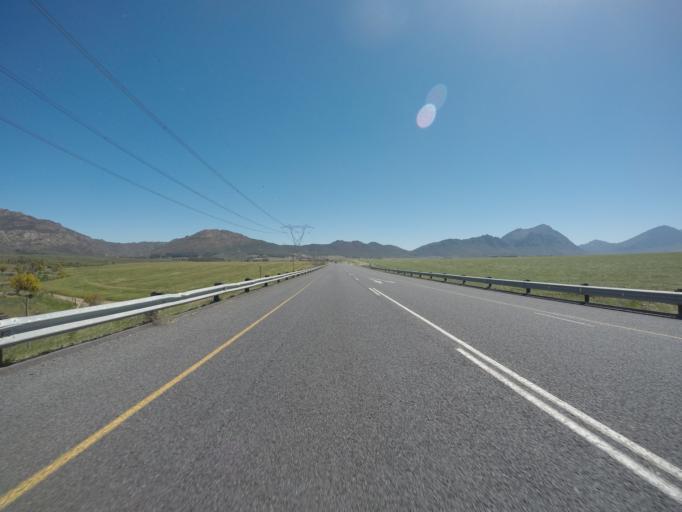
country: ZA
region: Western Cape
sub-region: Cape Winelands District Municipality
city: Ceres
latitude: -33.3133
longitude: 19.1238
